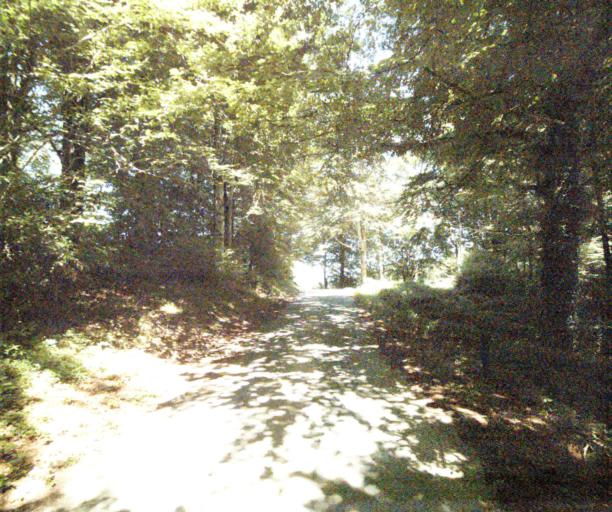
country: FR
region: Midi-Pyrenees
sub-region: Departement du Tarn
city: Dourgne
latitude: 43.4283
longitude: 2.1566
